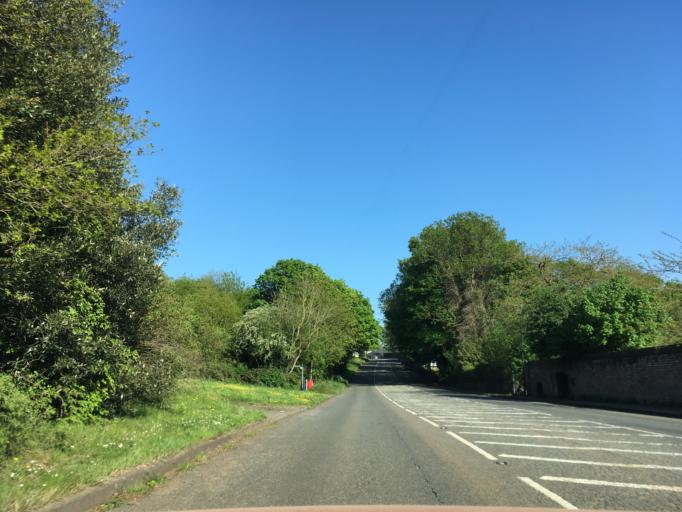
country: GB
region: Wales
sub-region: Monmouthshire
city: Chepstow
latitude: 51.6495
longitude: -2.6727
